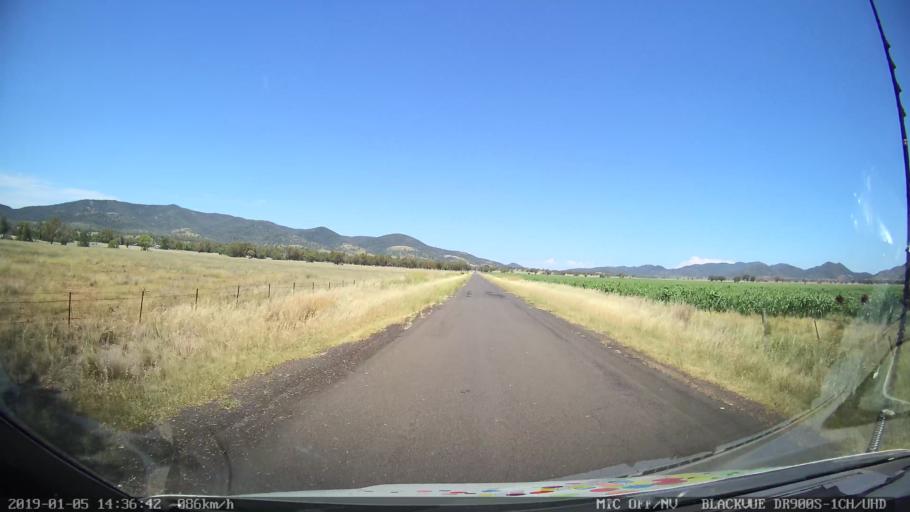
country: AU
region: New South Wales
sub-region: Tamworth Municipality
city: Phillip
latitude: -31.2452
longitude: 150.6679
